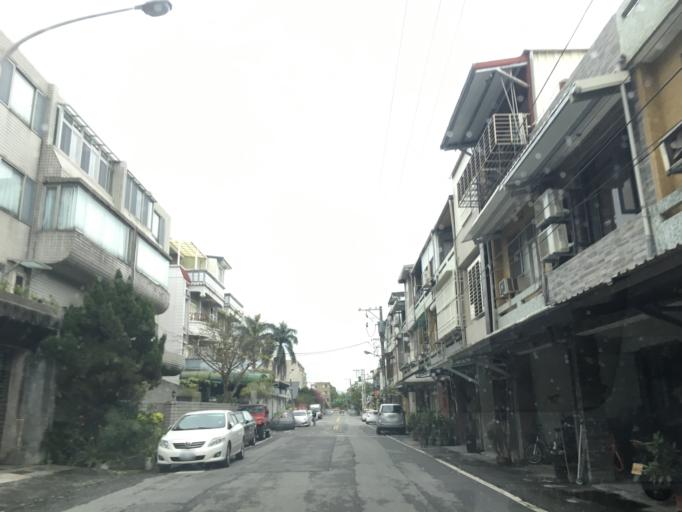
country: TW
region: Taiwan
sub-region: Hualien
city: Hualian
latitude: 23.9939
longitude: 121.5732
